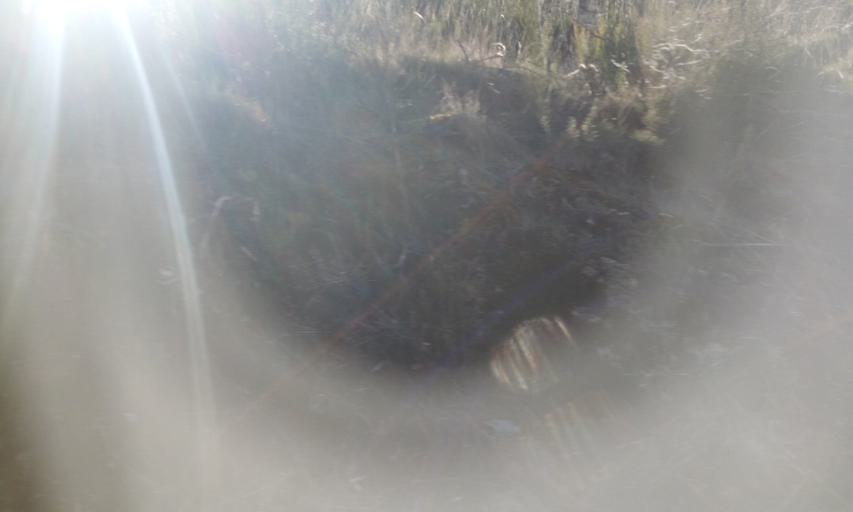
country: PT
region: Guarda
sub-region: Manteigas
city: Manteigas
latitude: 40.4858
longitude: -7.5185
